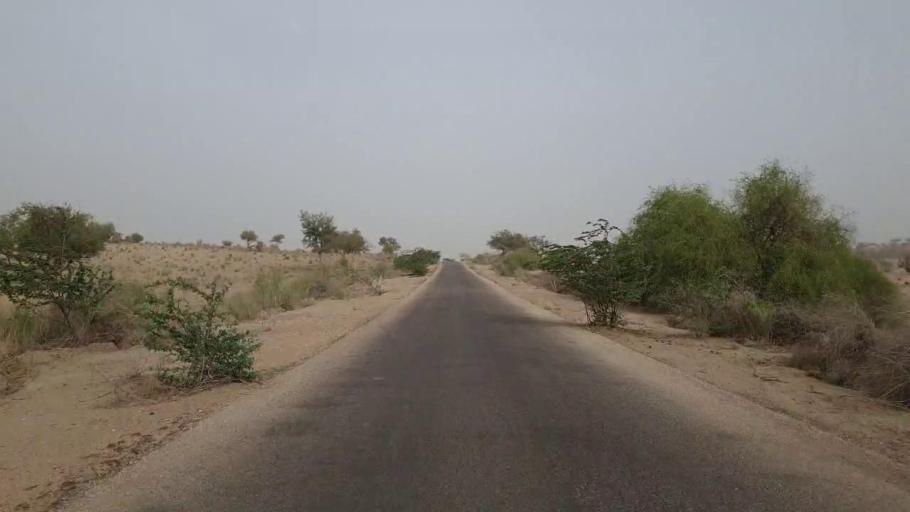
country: PK
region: Sindh
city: Islamkot
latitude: 24.5845
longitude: 70.2972
